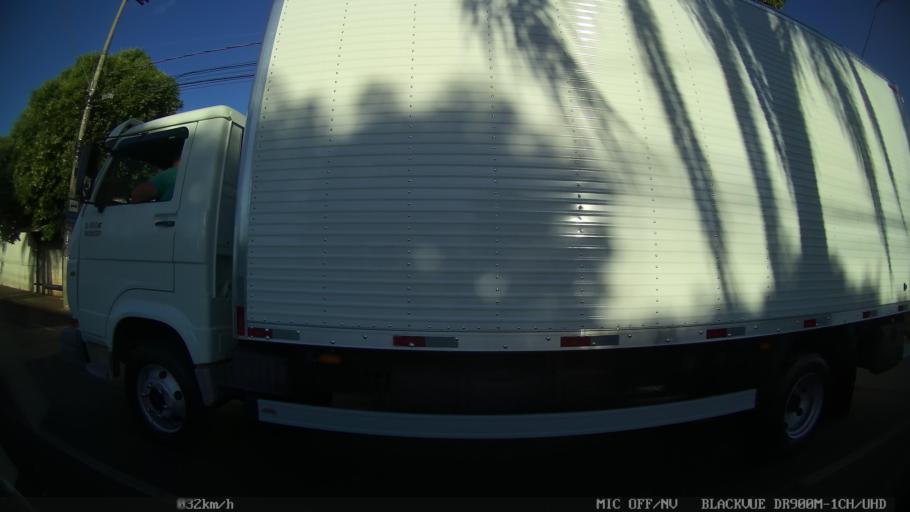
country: BR
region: Sao Paulo
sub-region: Sao Jose Do Rio Preto
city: Sao Jose do Rio Preto
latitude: -20.7756
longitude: -49.3659
